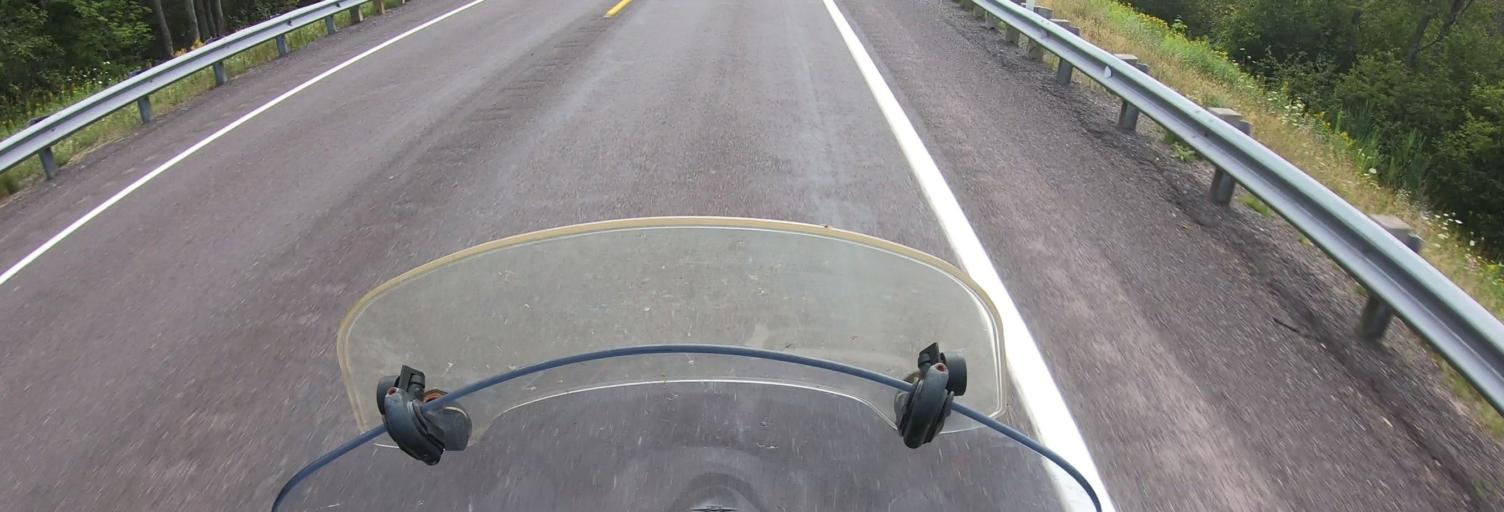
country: US
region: Michigan
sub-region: Houghton County
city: Hancock
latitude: 46.9231
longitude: -88.8120
